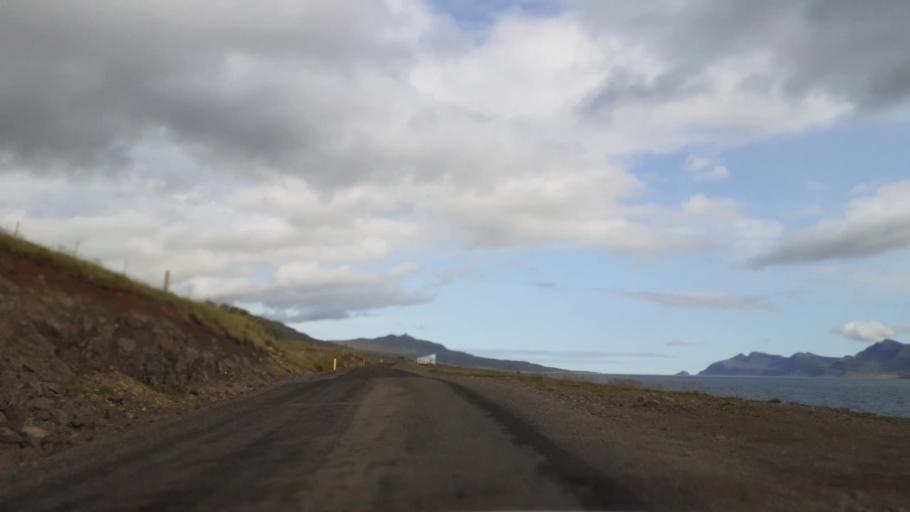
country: IS
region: East
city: Eskifjoerdur
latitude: 65.0554
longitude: -13.9733
